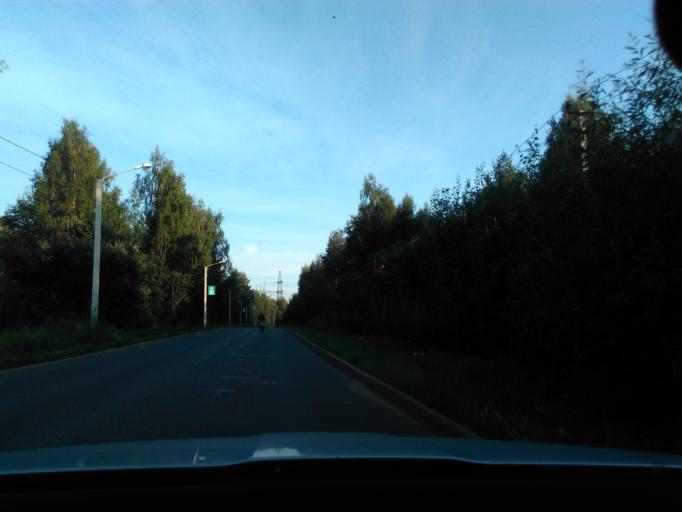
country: RU
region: Tverskaya
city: Konakovo
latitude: 56.7337
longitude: 36.7831
